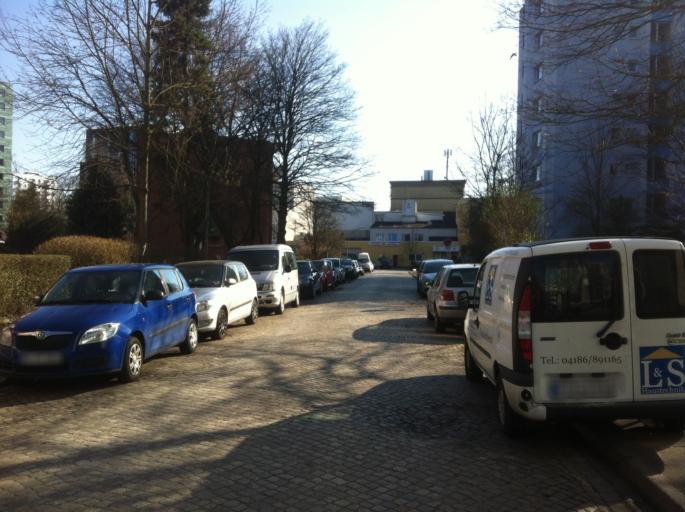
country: DE
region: Hamburg
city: St. Pauli
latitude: 53.5580
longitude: 9.9509
